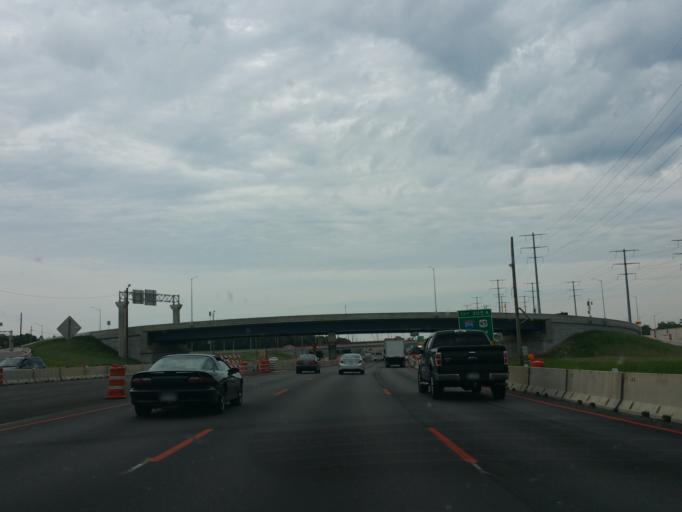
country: US
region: Wisconsin
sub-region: Waukesha County
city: Elm Grove
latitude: 43.0307
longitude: -88.0522
